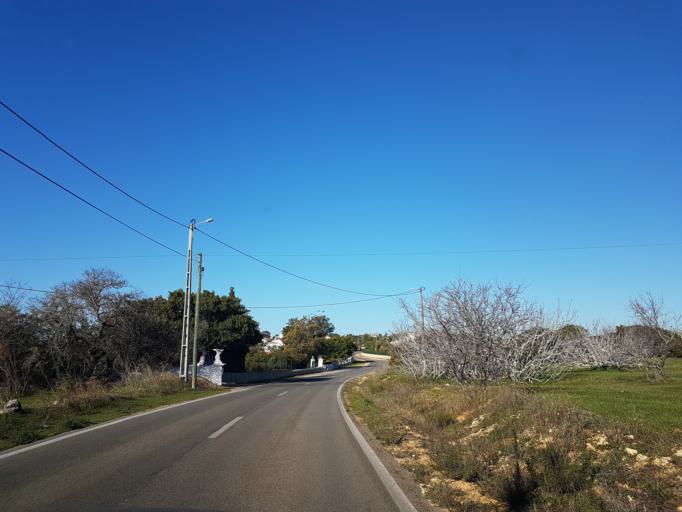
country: PT
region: Faro
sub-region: Lagoa
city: Carvoeiro
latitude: 37.0941
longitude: -8.4338
